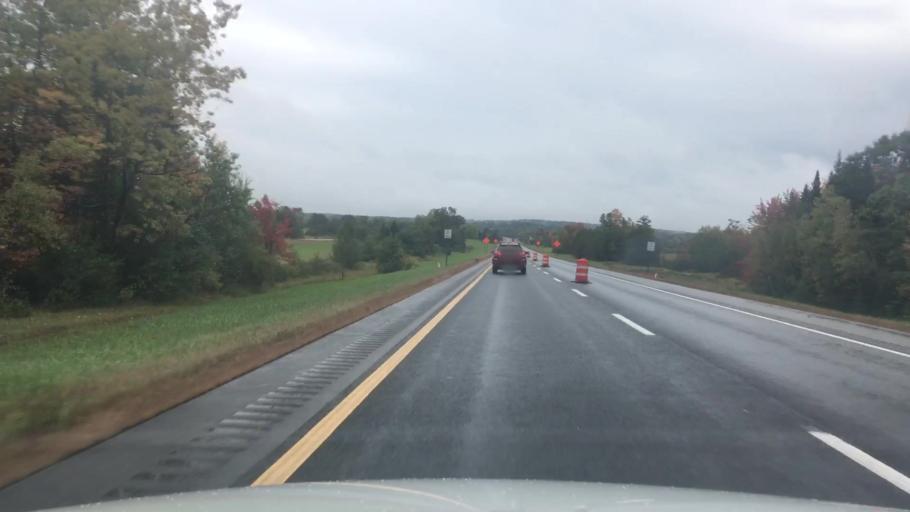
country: US
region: Maine
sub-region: Sagadahoc County
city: Richmond
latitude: 44.1434
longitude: -69.8413
